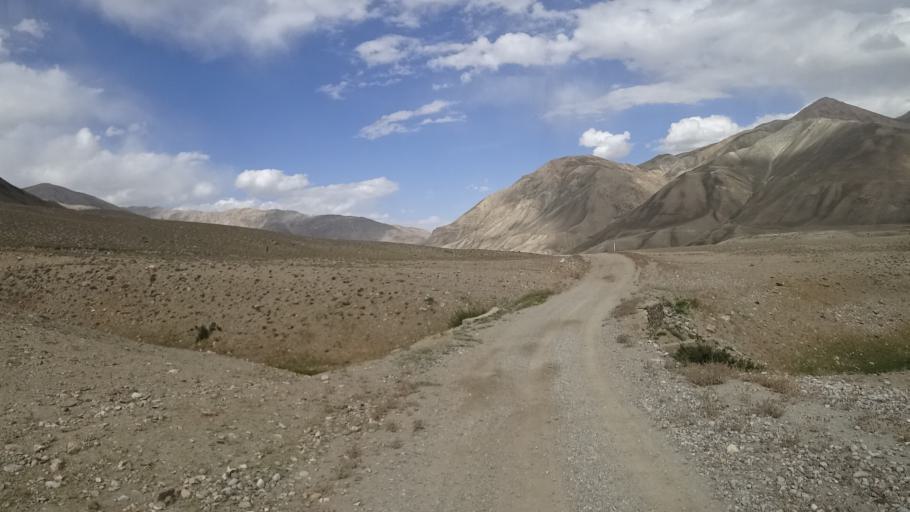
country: AF
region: Badakhshan
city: Khandud
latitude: 37.1935
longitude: 72.7661
